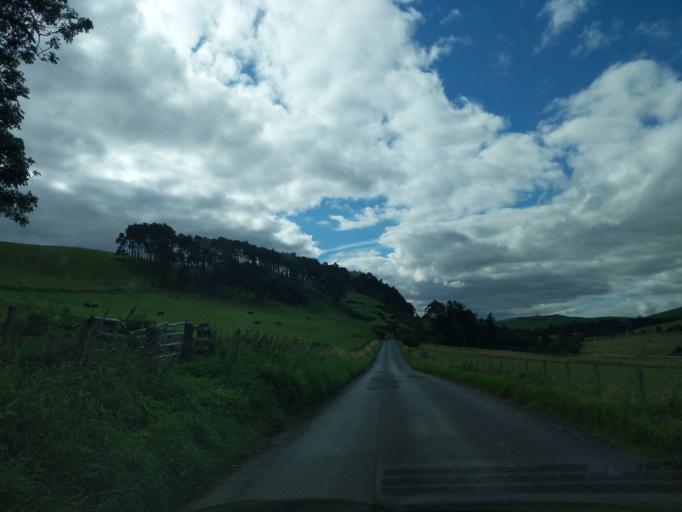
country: GB
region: Scotland
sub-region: The Scottish Borders
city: West Linton
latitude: 55.7128
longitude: -3.3352
